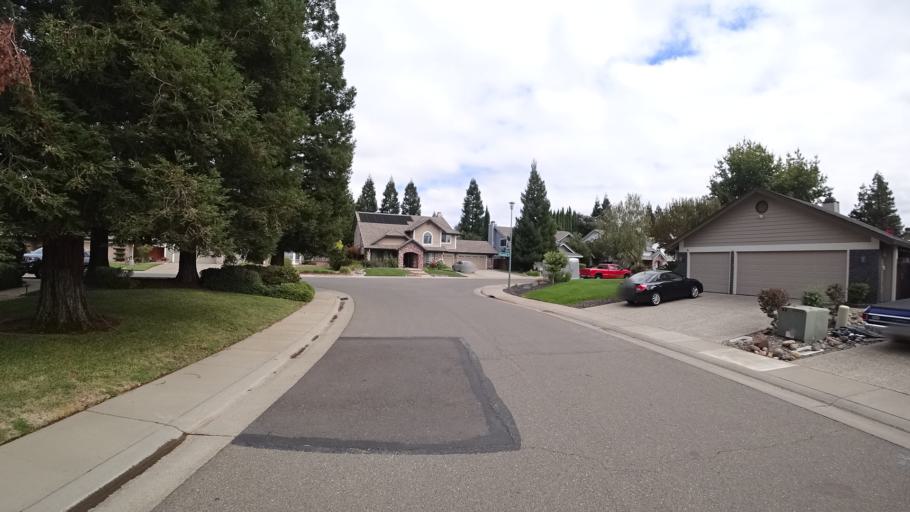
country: US
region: California
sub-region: Sacramento County
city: Laguna
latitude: 38.4182
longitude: -121.4385
